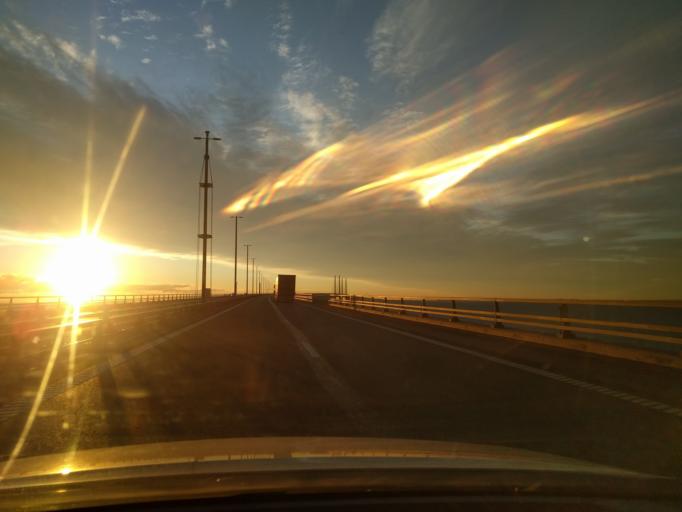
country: SE
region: Skane
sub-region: Malmo
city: Bunkeflostrand
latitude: 55.5661
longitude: 12.8888
